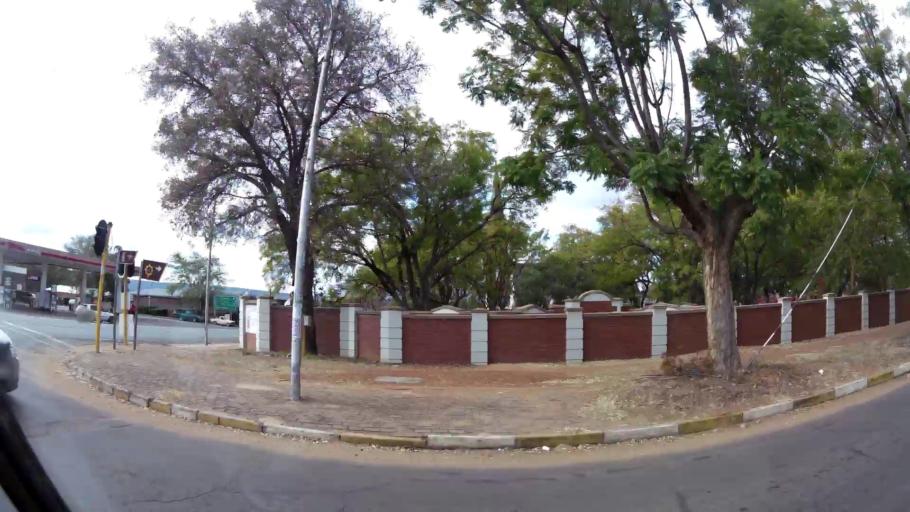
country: ZA
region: Limpopo
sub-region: Waterberg District Municipality
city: Modimolle
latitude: -24.7015
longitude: 28.4043
